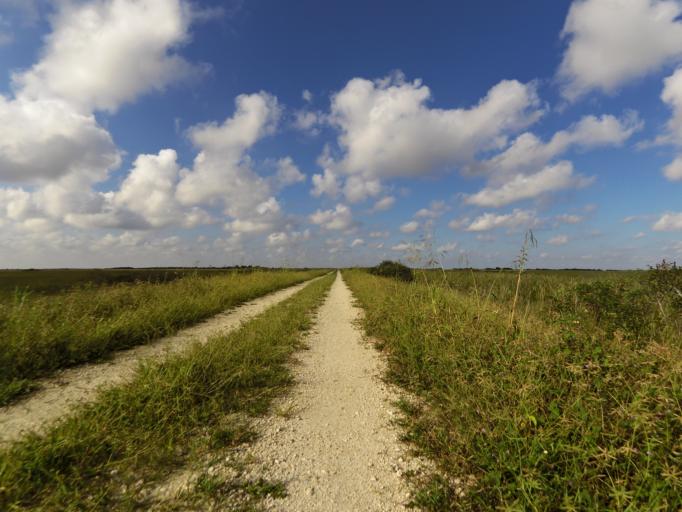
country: US
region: Florida
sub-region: Broward County
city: Weston
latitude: 26.0589
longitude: -80.4500
